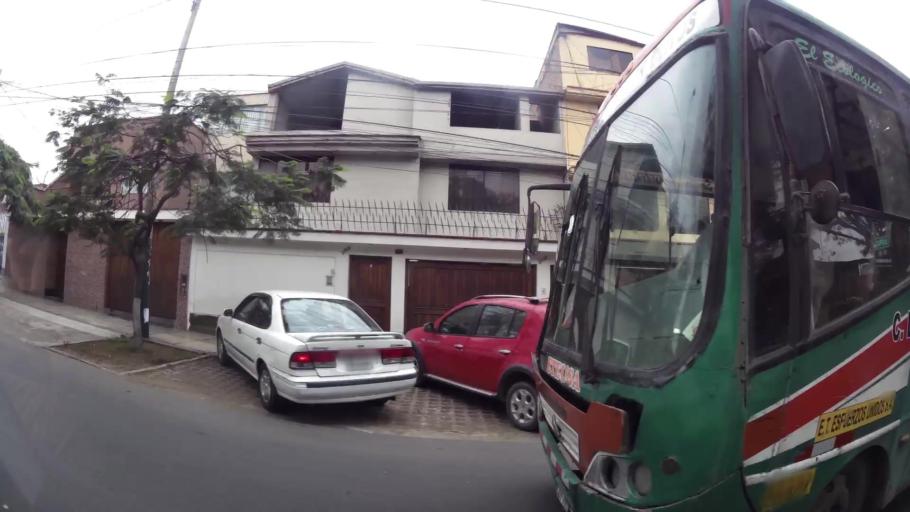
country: PE
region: Lima
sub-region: Lima
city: Surco
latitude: -12.1367
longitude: -76.9840
